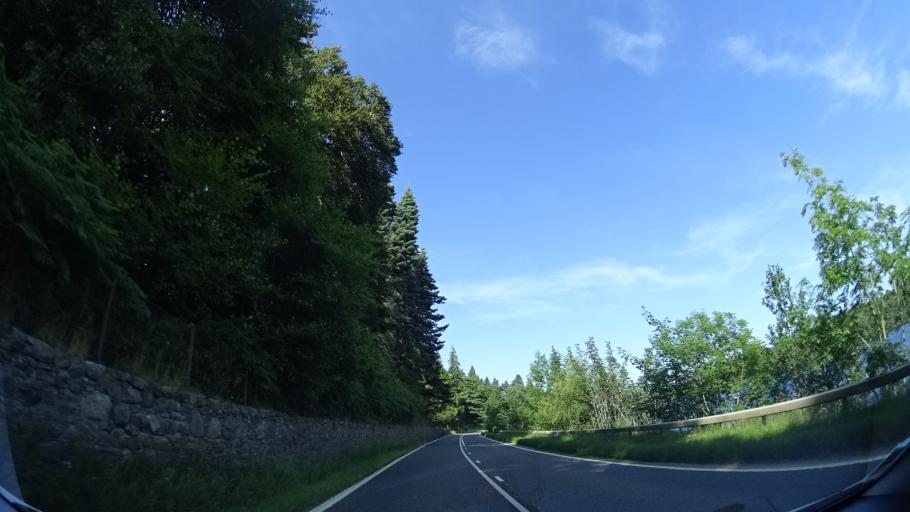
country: GB
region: Scotland
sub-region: Highland
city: Inverness
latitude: 57.4183
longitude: -4.3275
